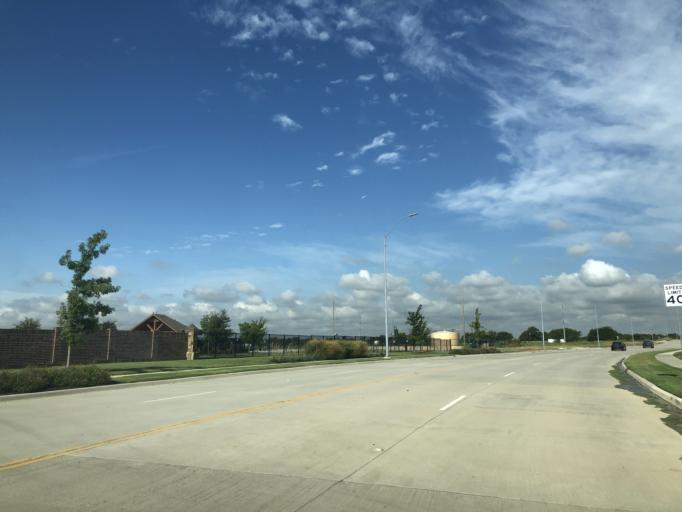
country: US
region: Texas
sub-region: Tarrant County
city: Haslet
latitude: 33.0184
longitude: -97.3081
